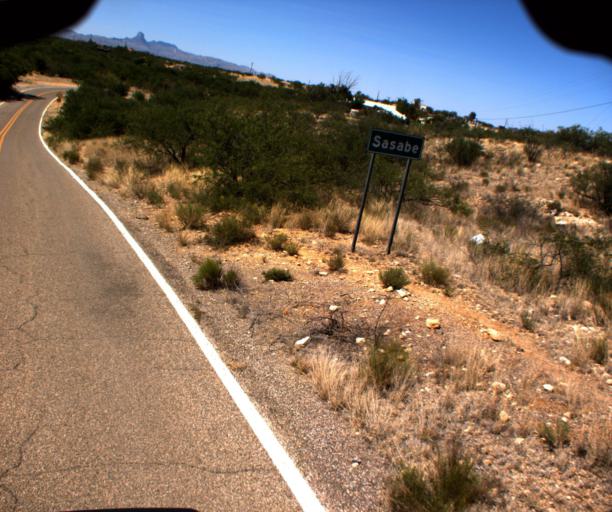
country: US
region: Arizona
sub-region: Santa Cruz County
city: Tubac
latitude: 31.4856
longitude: -111.5436
